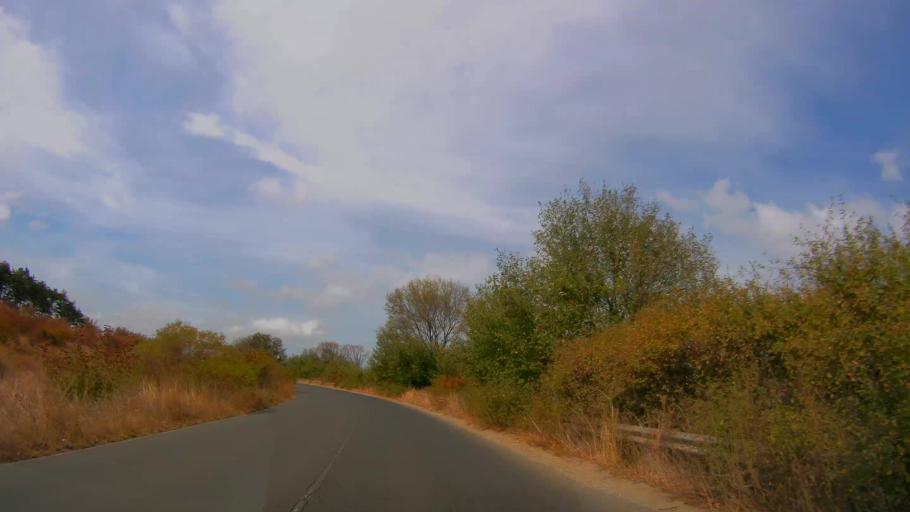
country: BG
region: Burgas
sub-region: Obshtina Sozopol
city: Sozopol
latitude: 42.4094
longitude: 27.6961
